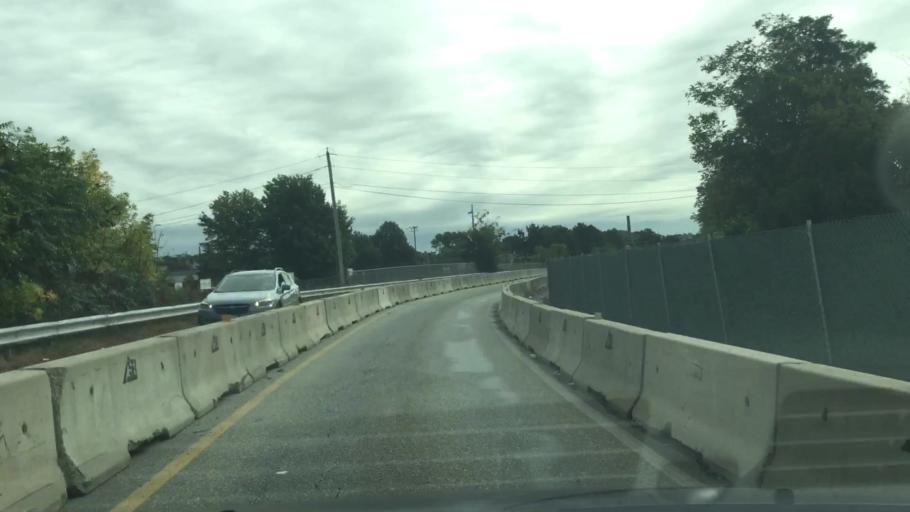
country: US
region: Massachusetts
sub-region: Middlesex County
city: Dracut
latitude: 42.6588
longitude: -71.3171
